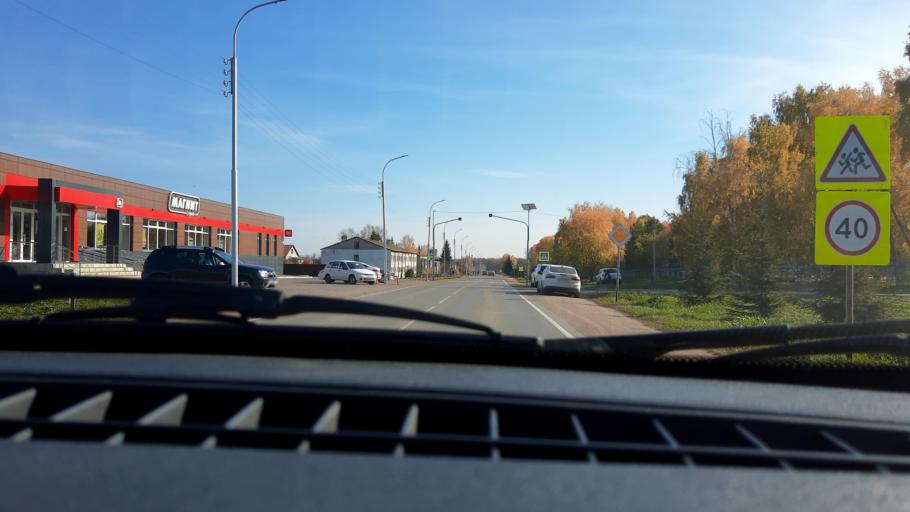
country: RU
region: Bashkortostan
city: Mikhaylovka
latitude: 54.8142
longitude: 55.8015
